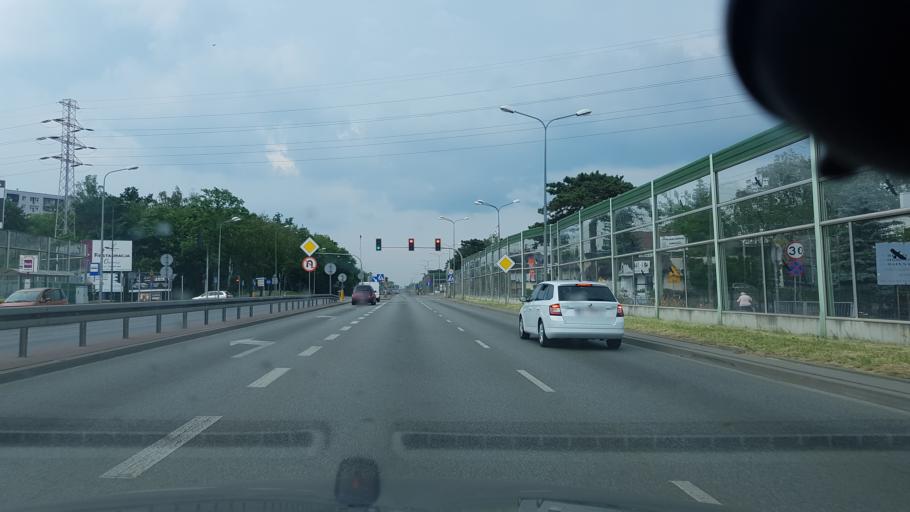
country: PL
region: Masovian Voivodeship
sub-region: Powiat legionowski
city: Jablonna
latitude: 52.3873
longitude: 20.9283
